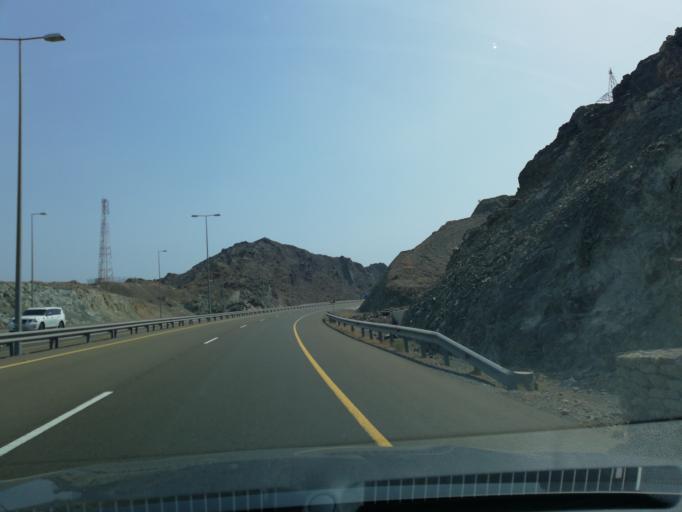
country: OM
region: Al Batinah
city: Al Liwa'
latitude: 24.2388
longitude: 56.3477
